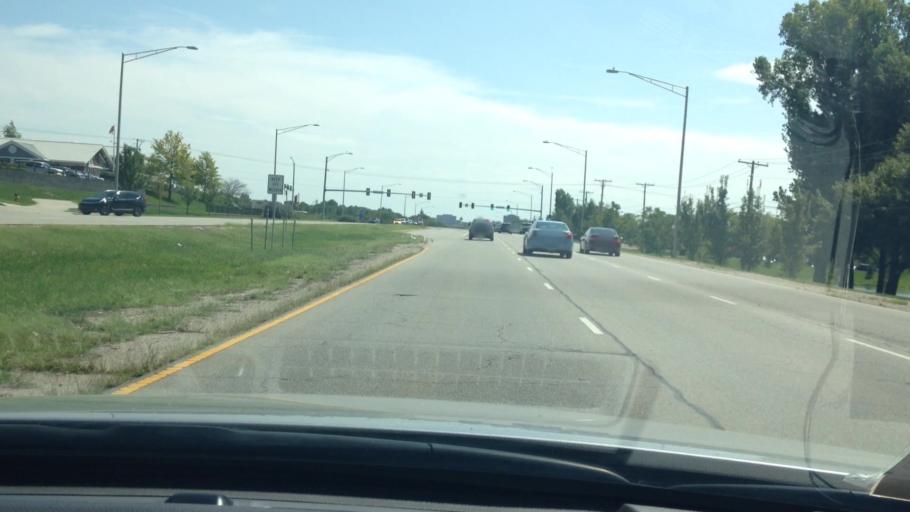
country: US
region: Kansas
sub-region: Johnson County
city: Overland Park
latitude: 38.9585
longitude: -94.6677
